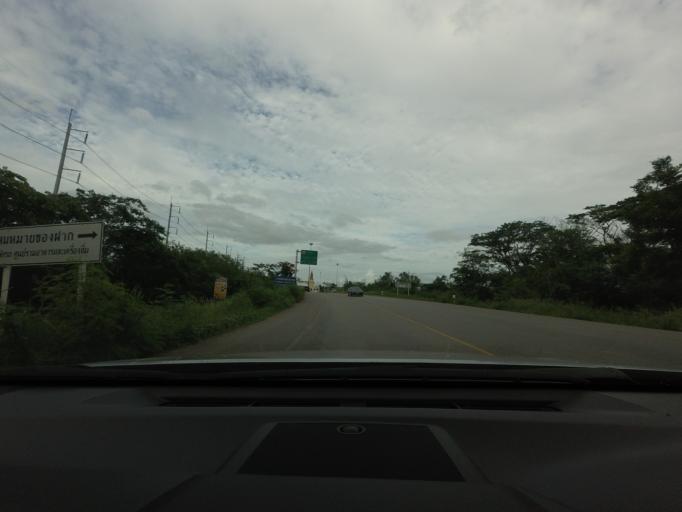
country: TH
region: Prachuap Khiri Khan
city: Hua Hin
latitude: 12.5767
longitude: 99.8637
